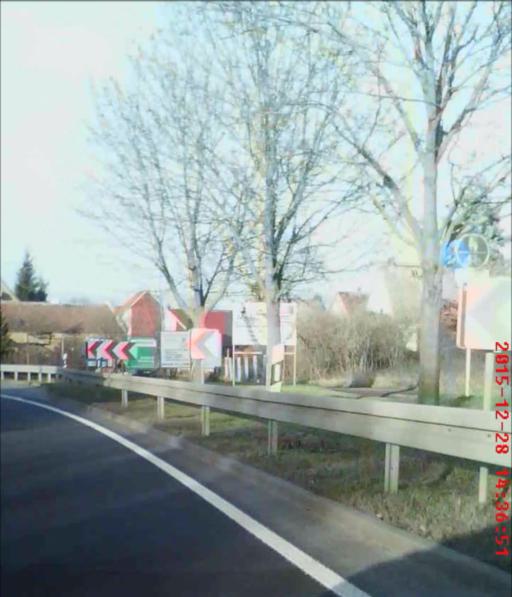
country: DE
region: Thuringia
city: Buttelstedt
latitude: 51.0608
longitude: 11.3410
